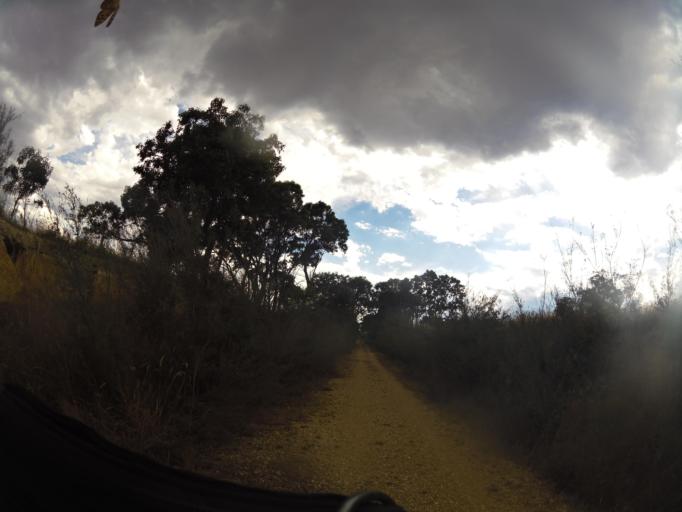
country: AU
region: Victoria
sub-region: Wellington
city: Heyfield
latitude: -38.0244
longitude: 146.6724
